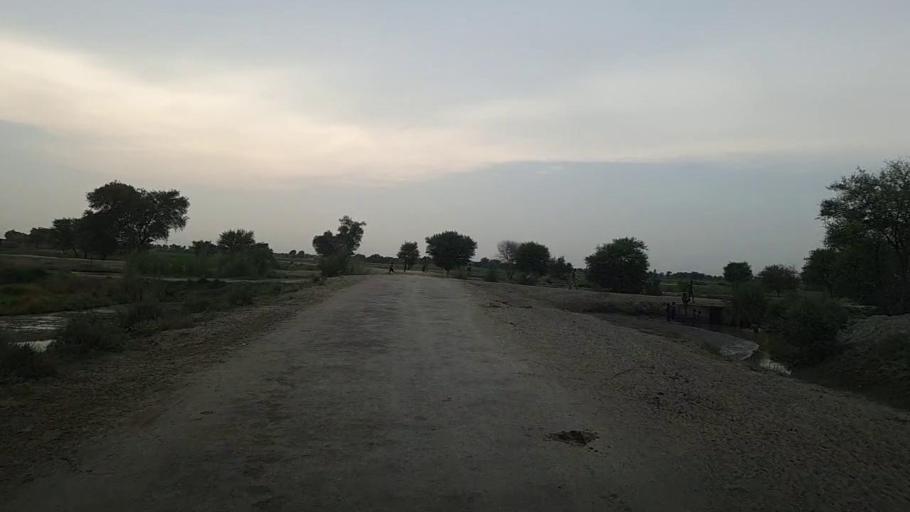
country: PK
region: Sindh
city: Khanpur
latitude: 27.8466
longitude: 69.4564
